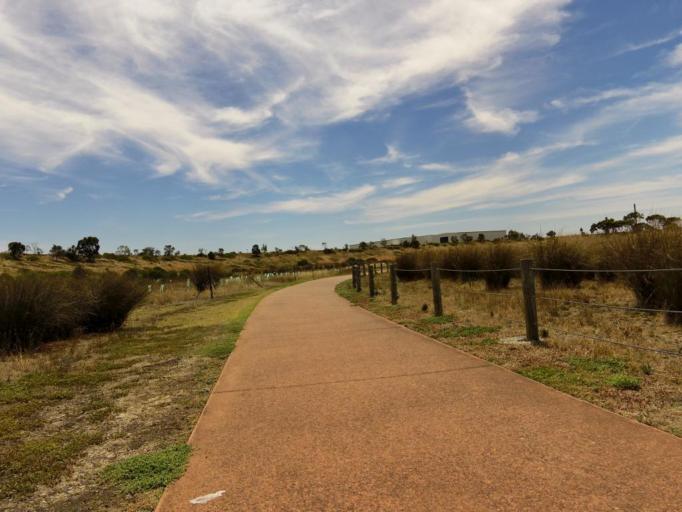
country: AU
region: Victoria
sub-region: Hobsons Bay
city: Altona
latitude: -37.8558
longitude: 144.8299
